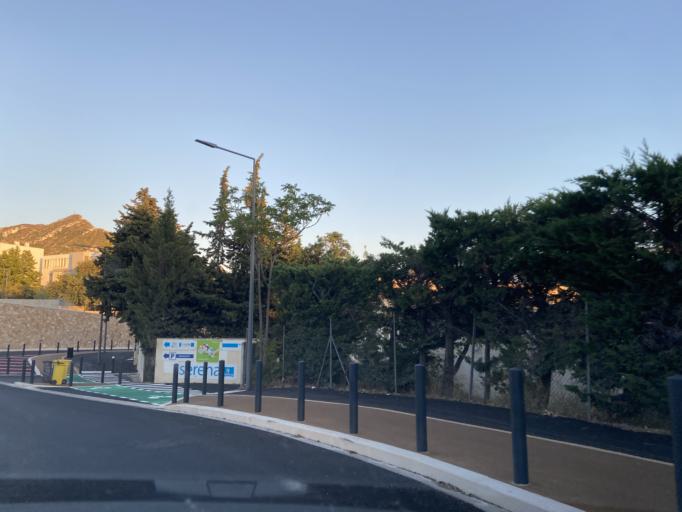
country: FR
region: Provence-Alpes-Cote d'Azur
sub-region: Departement des Bouches-du-Rhone
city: Marseille 10
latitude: 43.2752
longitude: 5.4240
